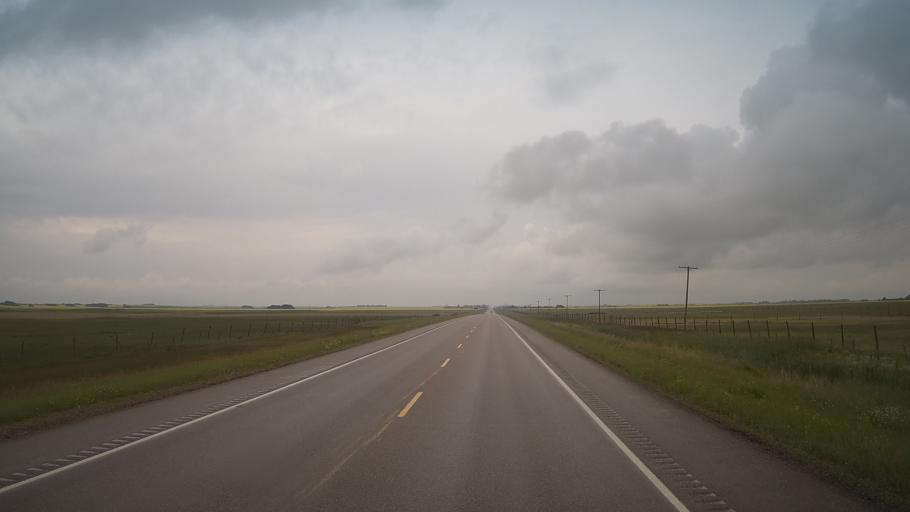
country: CA
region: Saskatchewan
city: Unity
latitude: 52.4346
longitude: -108.9848
